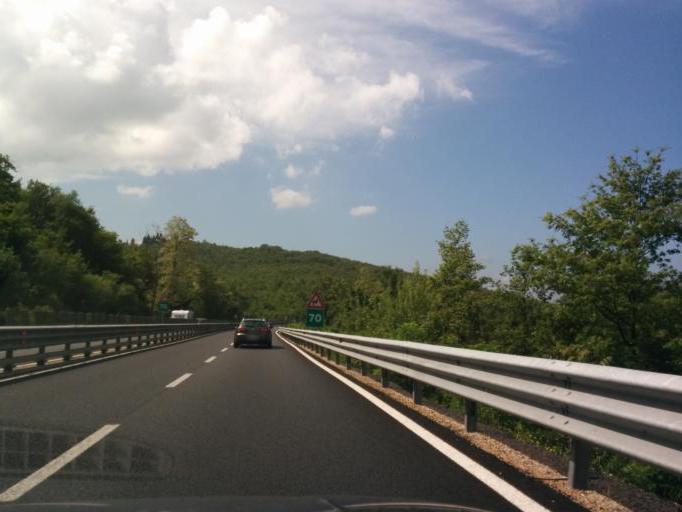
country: IT
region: Tuscany
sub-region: Province of Florence
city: Barberino Val d'Elsa
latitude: 43.5177
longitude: 11.1970
